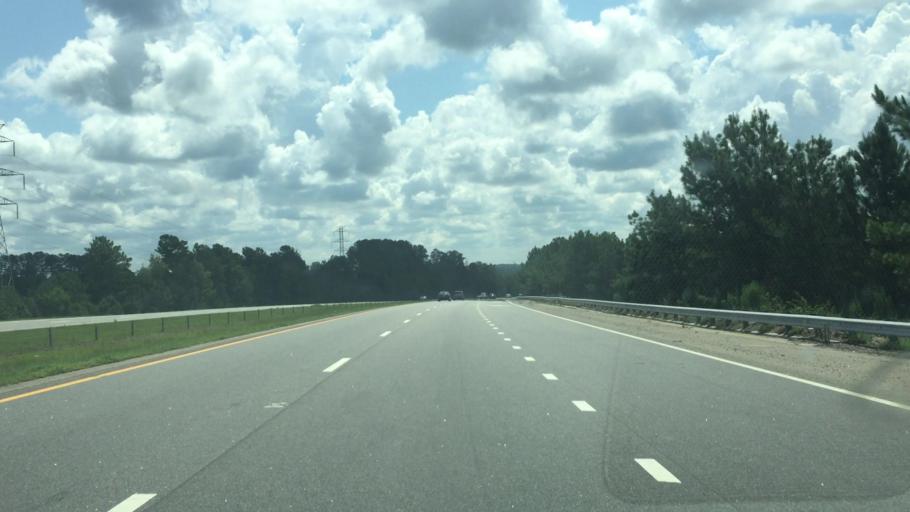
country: US
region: North Carolina
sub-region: Richmond County
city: Cordova
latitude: 34.9299
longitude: -79.8265
